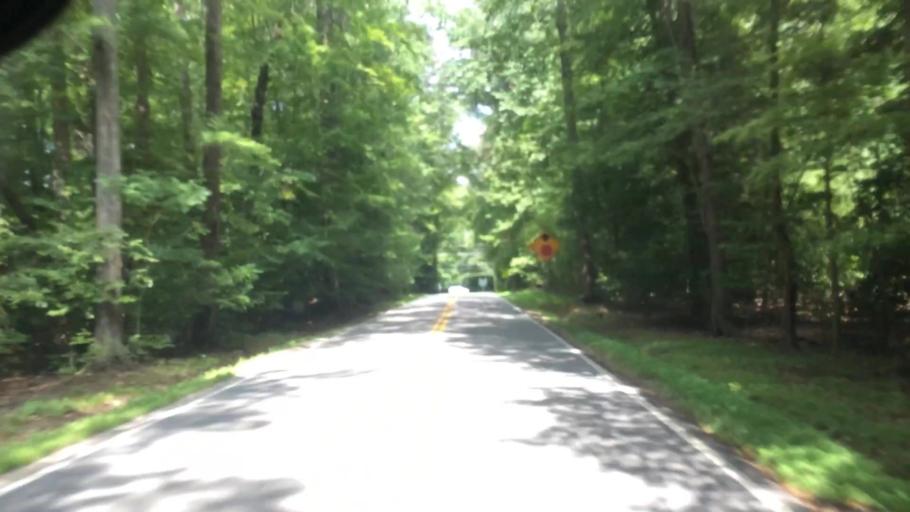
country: US
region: Virginia
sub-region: James City County
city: Williamsburg
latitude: 37.2516
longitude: -76.7995
